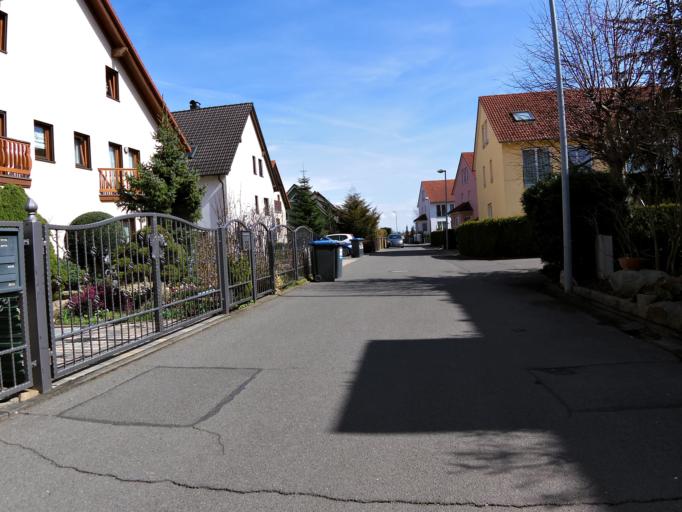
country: DE
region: Saxony
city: Borsdorf
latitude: 51.3407
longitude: 12.4927
